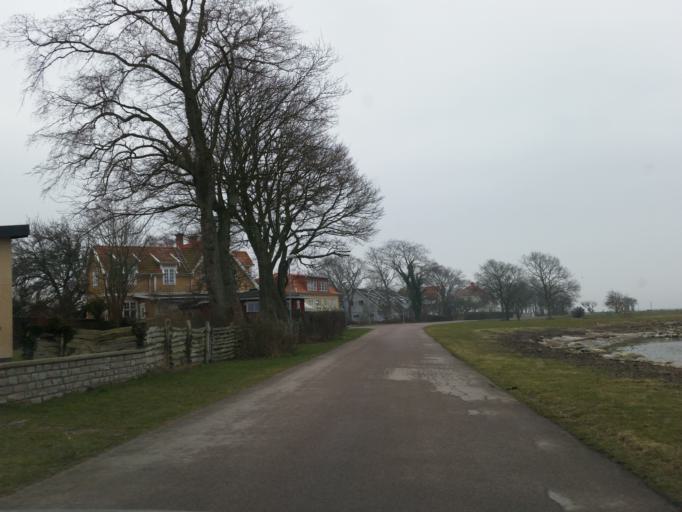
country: SE
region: Kalmar
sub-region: Morbylanga Kommun
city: Moerbylanga
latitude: 56.5250
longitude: 16.3717
